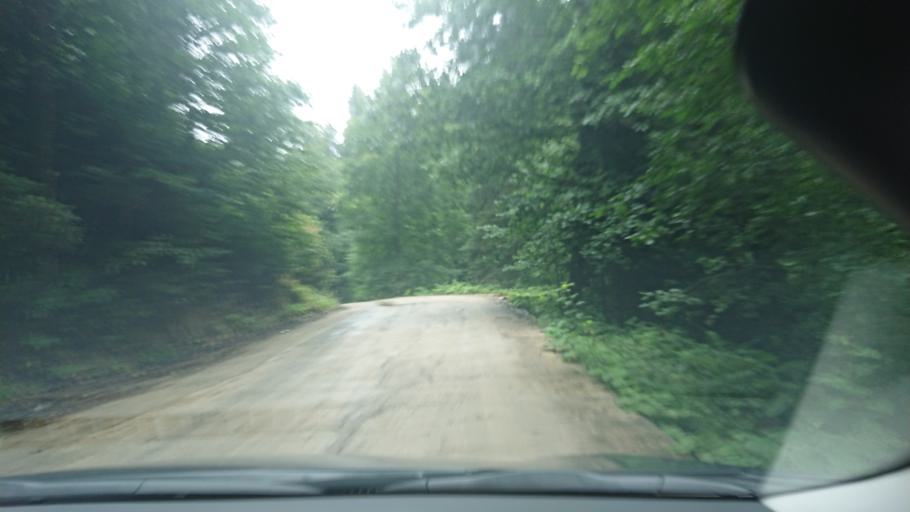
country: TR
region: Gumushane
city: Kurtun
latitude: 40.6595
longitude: 39.0258
